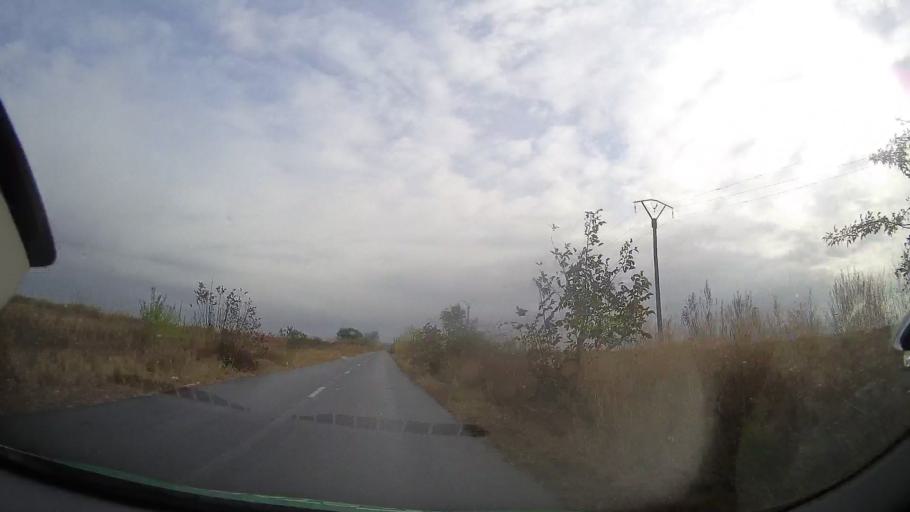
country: RO
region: Ialomita
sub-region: Comuna Maia
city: Maia
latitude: 44.7471
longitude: 26.3963
